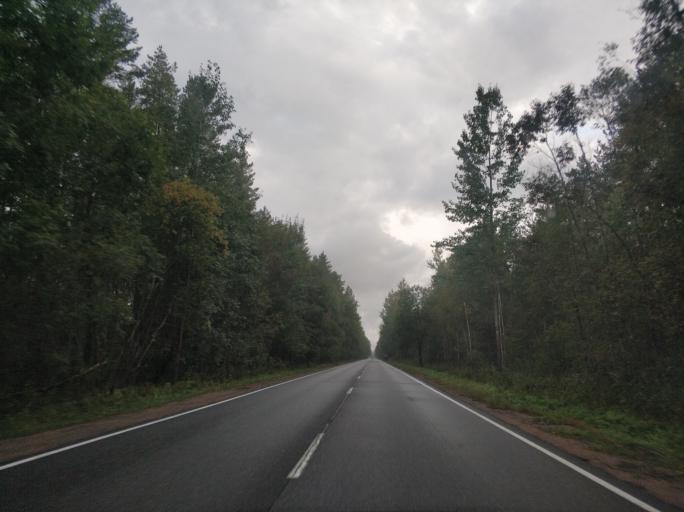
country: RU
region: Leningrad
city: Borisova Griva
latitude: 60.1452
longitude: 30.9451
